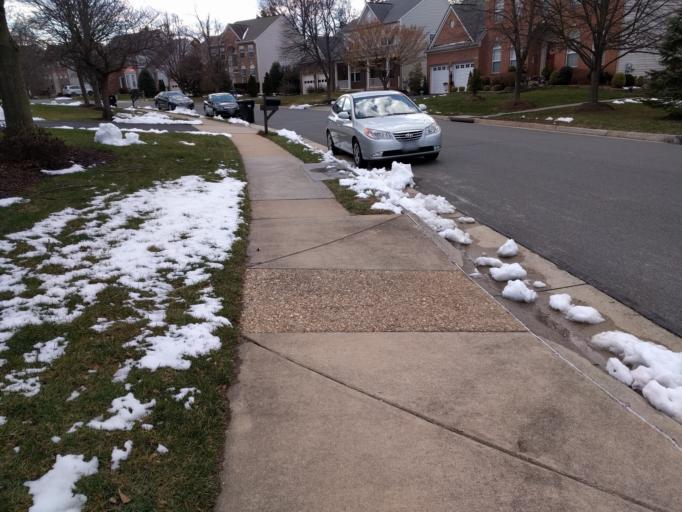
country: US
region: Virginia
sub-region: Loudoun County
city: Sugarland Run
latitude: 39.0227
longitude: -77.3813
